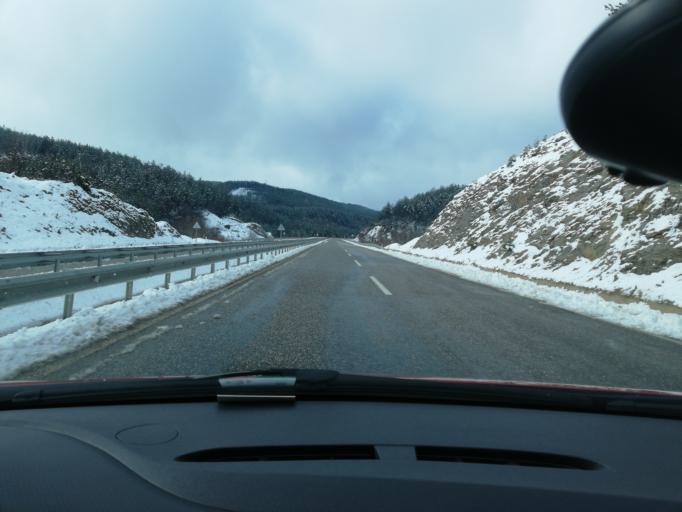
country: TR
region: Kastamonu
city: Akkaya
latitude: 41.2838
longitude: 33.4323
